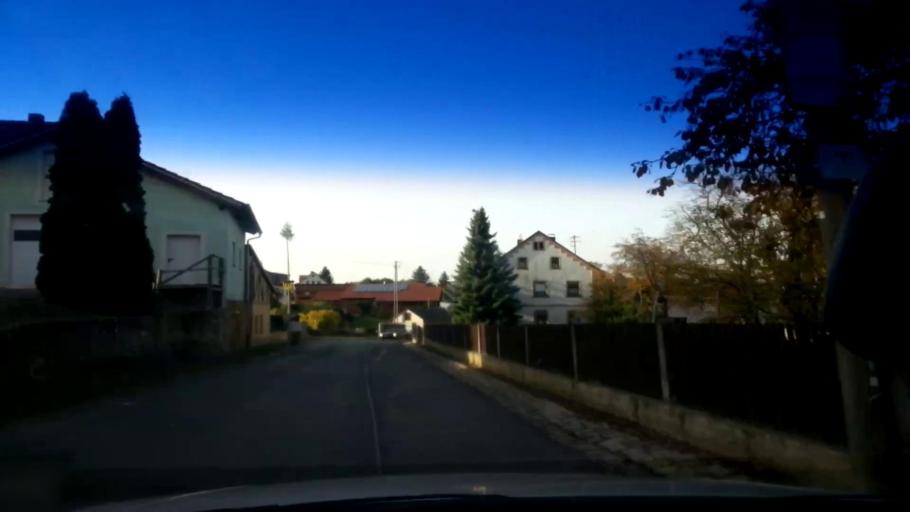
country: DE
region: Bavaria
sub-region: Upper Franconia
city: Schesslitz
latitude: 49.9599
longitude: 11.0577
